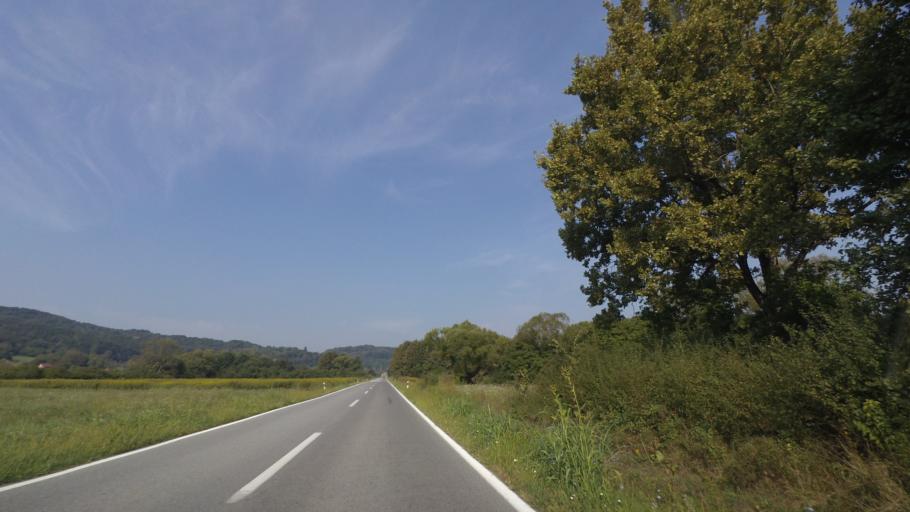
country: HR
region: Pozesko-Slavonska
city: Lipik
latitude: 45.4187
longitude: 17.1194
